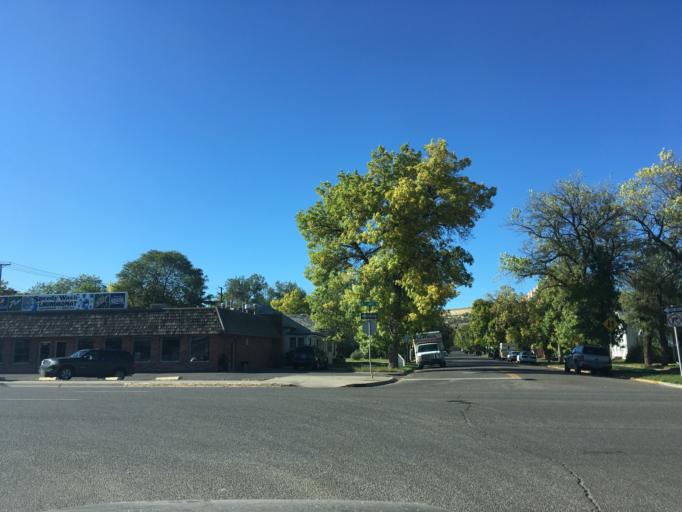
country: US
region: Montana
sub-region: Yellowstone County
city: Billings
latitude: 45.7881
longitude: -108.5063
